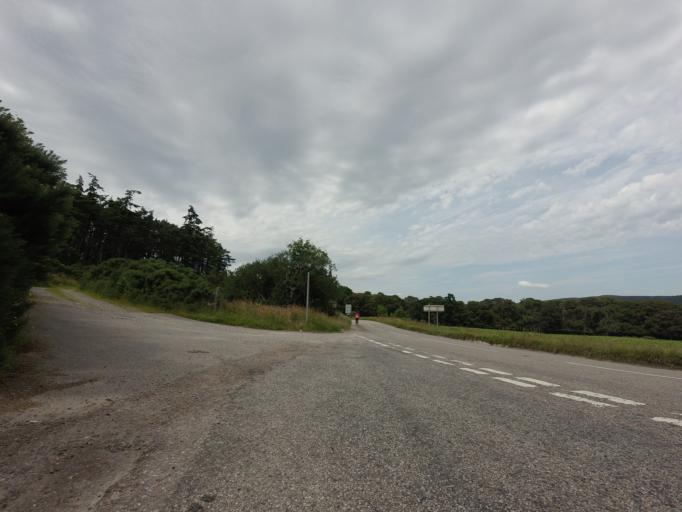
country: GB
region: Scotland
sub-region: Highland
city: Alness
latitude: 57.8537
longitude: -4.3047
